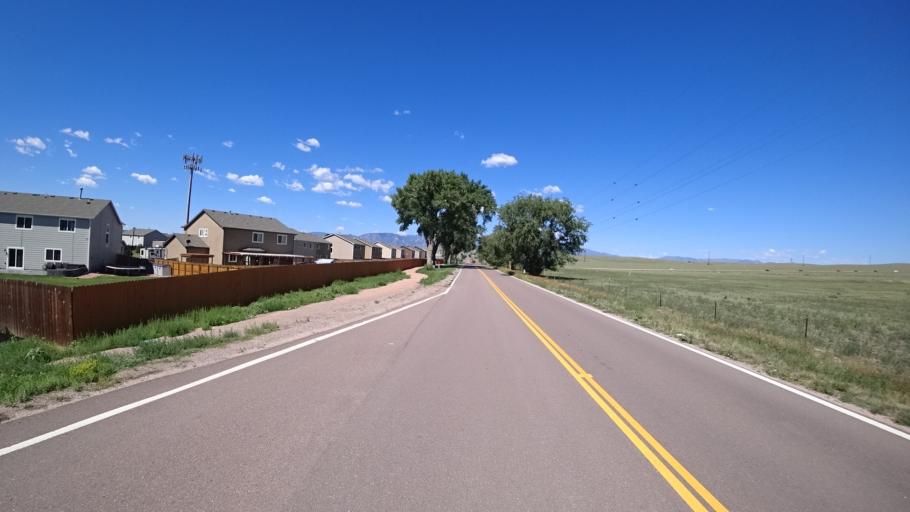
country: US
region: Colorado
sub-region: El Paso County
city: Security-Widefield
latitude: 38.7810
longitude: -104.6543
